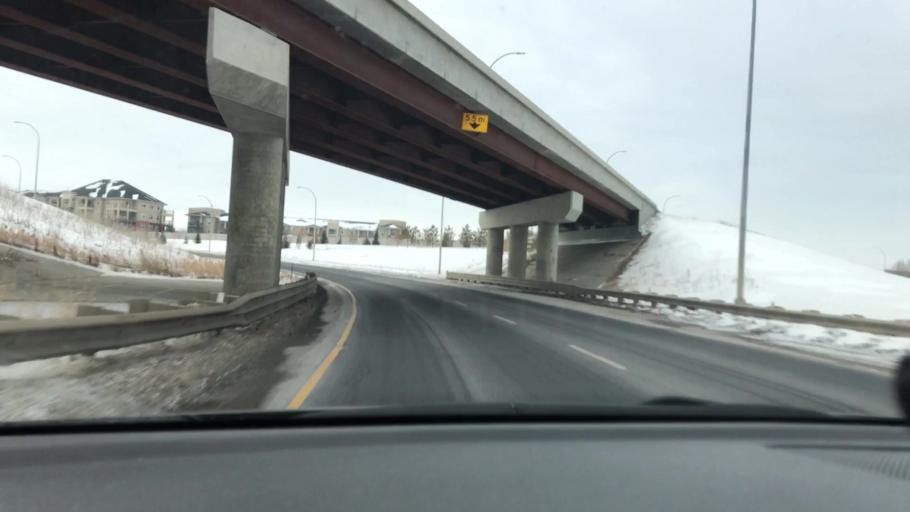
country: CA
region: Alberta
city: Edmonton
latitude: 53.5160
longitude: -113.4308
